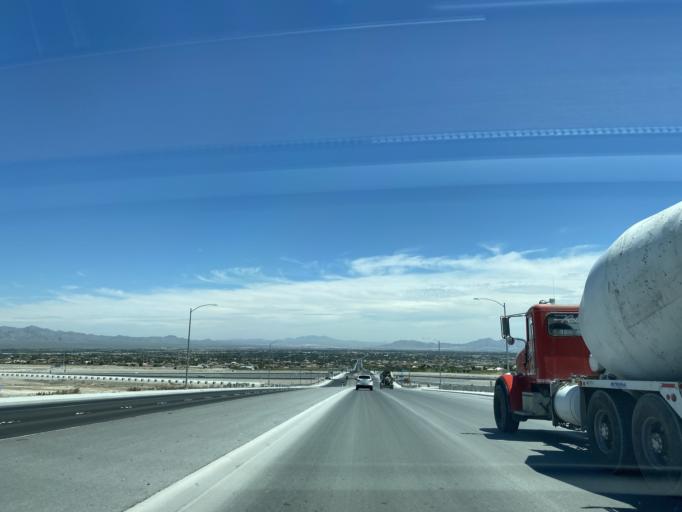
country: US
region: Nevada
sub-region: Clark County
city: Summerlin South
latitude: 36.2478
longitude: -115.3235
